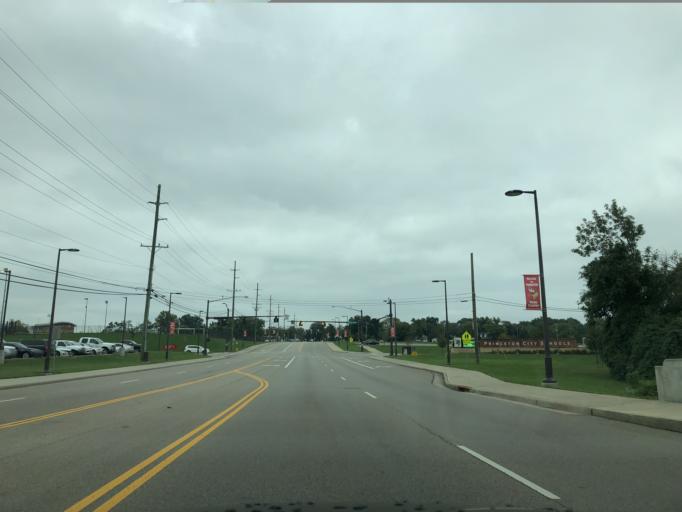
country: US
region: Ohio
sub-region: Hamilton County
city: Glendale
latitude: 39.2742
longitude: -84.4442
